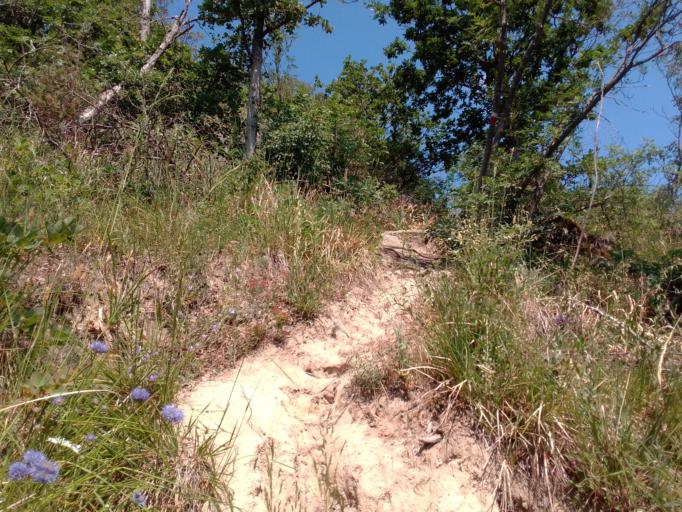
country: IT
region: Emilia-Romagna
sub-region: Provincia di Piacenza
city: Pecorara
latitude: 44.9061
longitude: 9.4093
